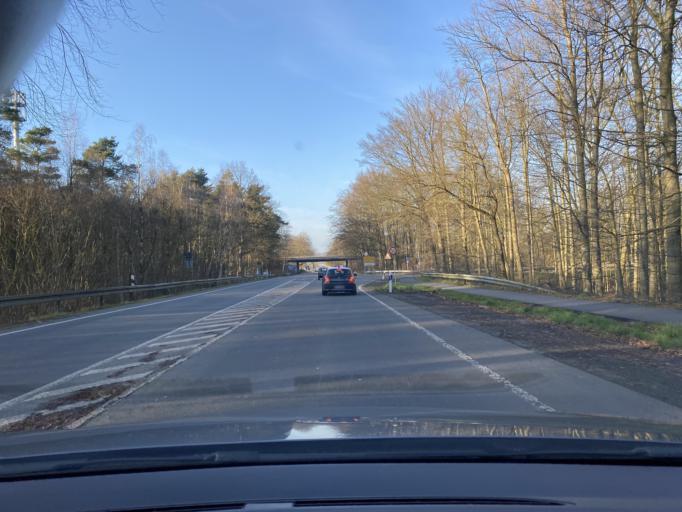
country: DE
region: North Rhine-Westphalia
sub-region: Regierungsbezirk Munster
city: Haltern
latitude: 51.7207
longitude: 7.1888
